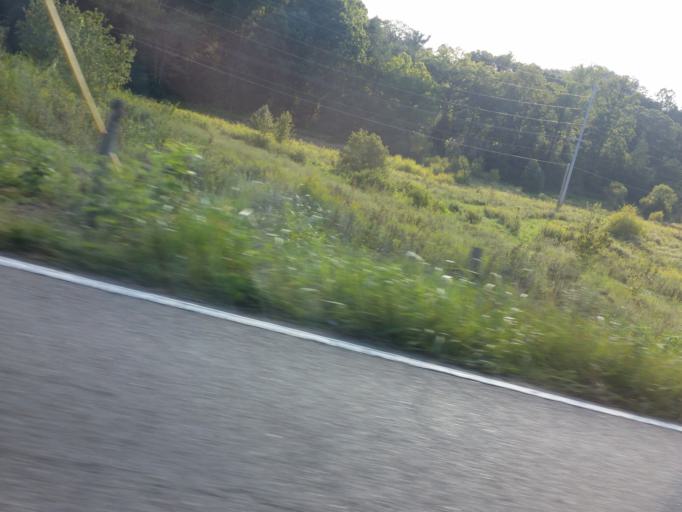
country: US
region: Tennessee
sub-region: Union County
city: Condon
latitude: 36.1901
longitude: -83.8176
